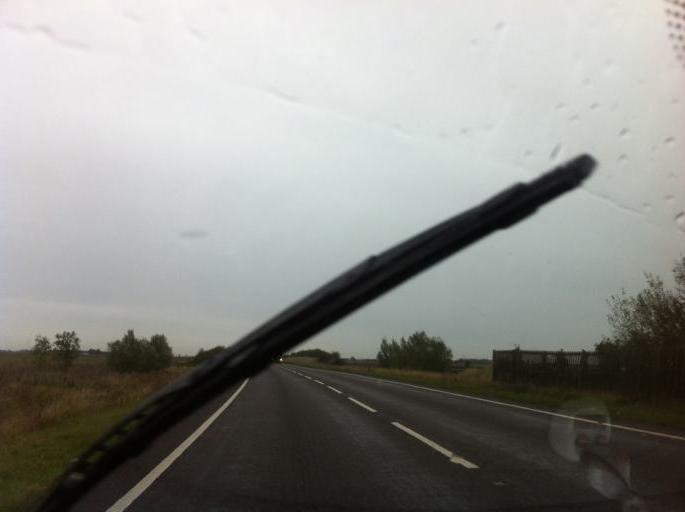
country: GB
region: England
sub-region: Peterborough
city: Eye
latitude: 52.6178
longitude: -0.2067
